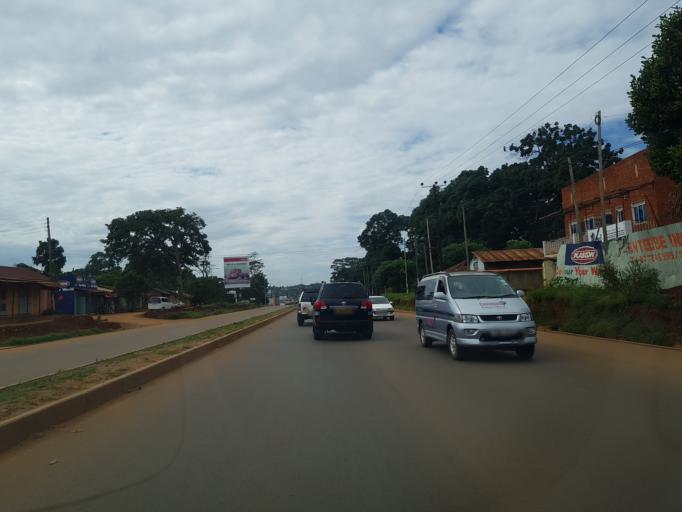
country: UG
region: Central Region
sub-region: Wakiso District
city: Entebbe
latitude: 0.0800
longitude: 32.4812
